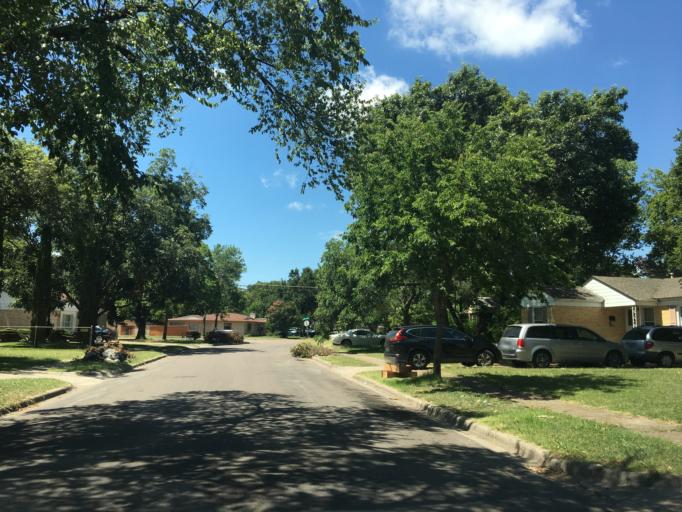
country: US
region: Texas
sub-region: Dallas County
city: Garland
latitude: 32.8385
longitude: -96.6810
